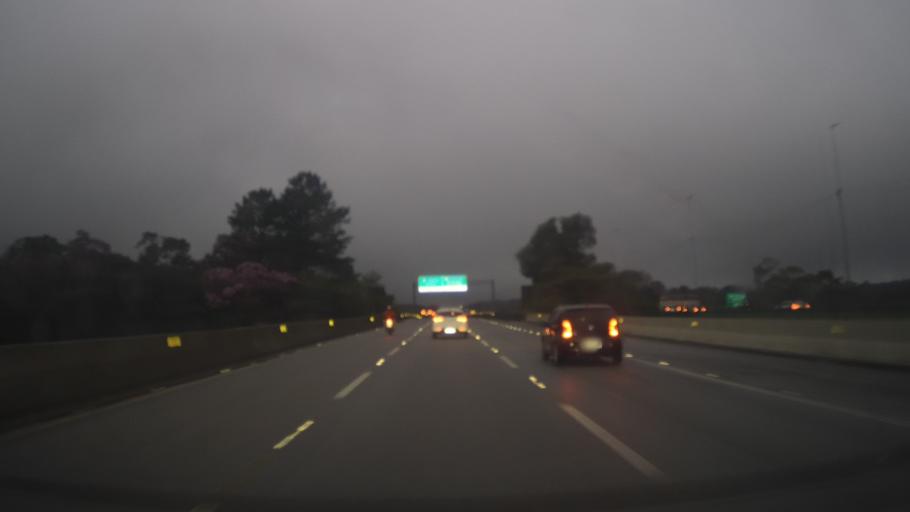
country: BR
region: Sao Paulo
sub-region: Cubatao
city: Cubatao
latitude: -23.8930
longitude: -46.5647
